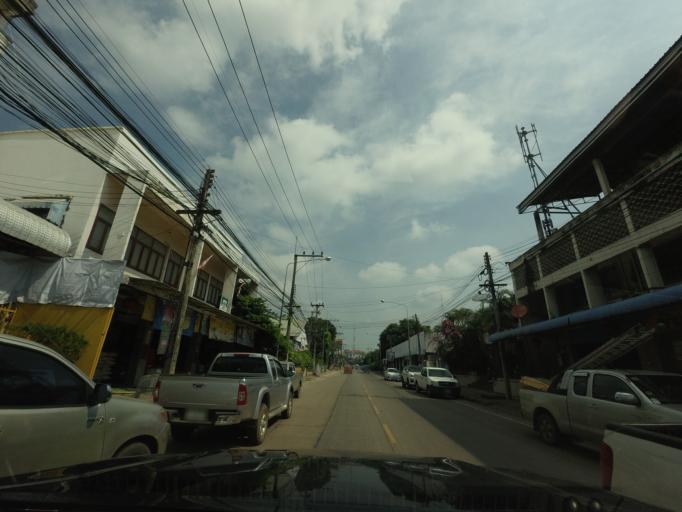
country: TH
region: Khon Kaen
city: Khon Kaen
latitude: 16.4350
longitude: 102.8297
